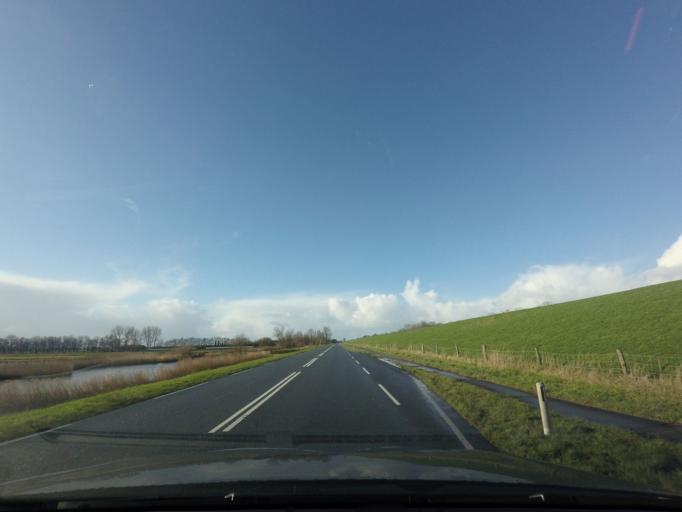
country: NL
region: North Holland
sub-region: Gemeente Opmeer
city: Opmeer
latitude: 52.7520
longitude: 4.9884
